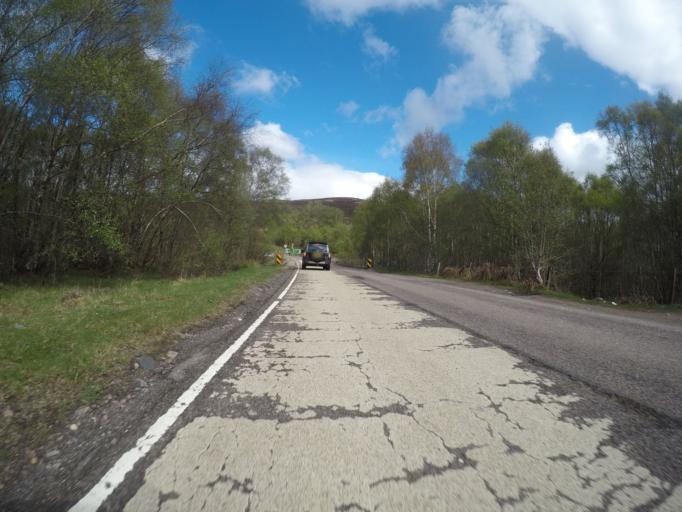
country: GB
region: Scotland
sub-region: Highland
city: Spean Bridge
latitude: 57.1453
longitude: -4.9583
